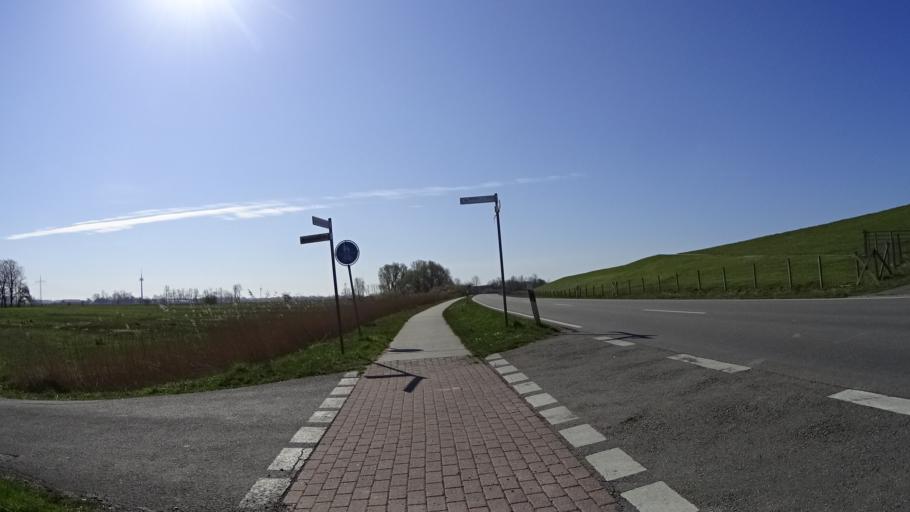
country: DE
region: Lower Saxony
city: Jemgum
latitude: 53.2787
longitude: 7.4065
